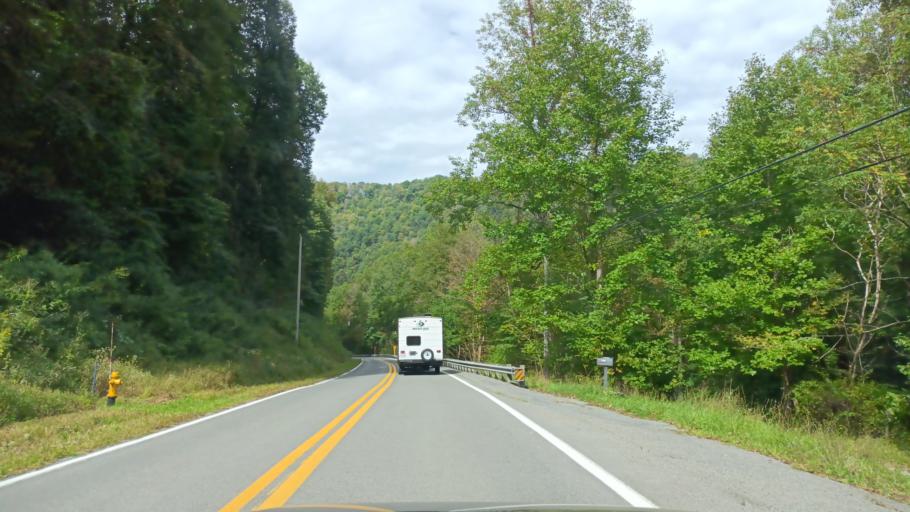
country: US
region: West Virginia
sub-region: Preston County
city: Kingwood
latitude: 39.3252
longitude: -79.6654
